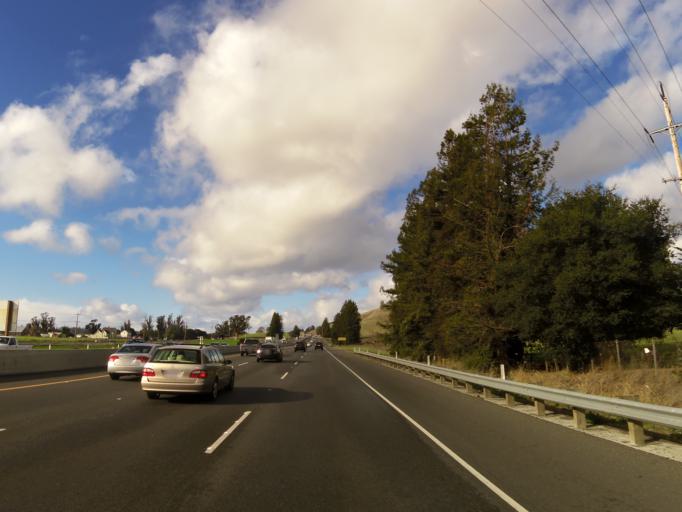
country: US
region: California
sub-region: Sonoma County
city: Penngrove
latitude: 38.2816
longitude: -122.6823
